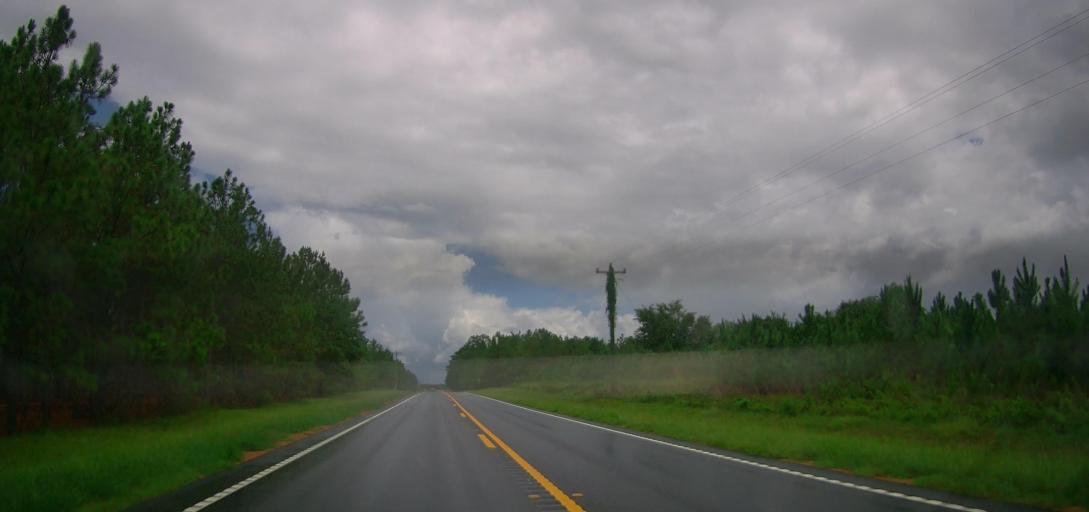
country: US
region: Georgia
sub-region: Pulaski County
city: Hawkinsville
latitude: 32.1127
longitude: -83.5772
